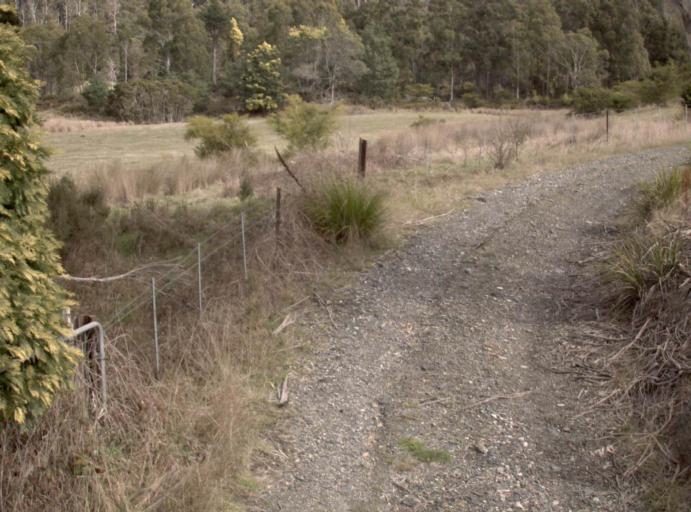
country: AU
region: Tasmania
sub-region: Launceston
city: Mayfield
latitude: -41.2709
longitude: 147.1614
